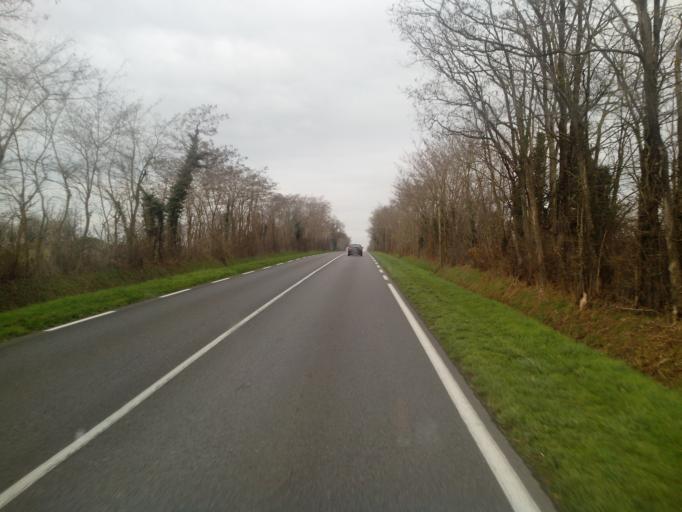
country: FR
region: Poitou-Charentes
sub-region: Departement de la Vienne
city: Saulge
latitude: 46.3367
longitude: 0.8047
